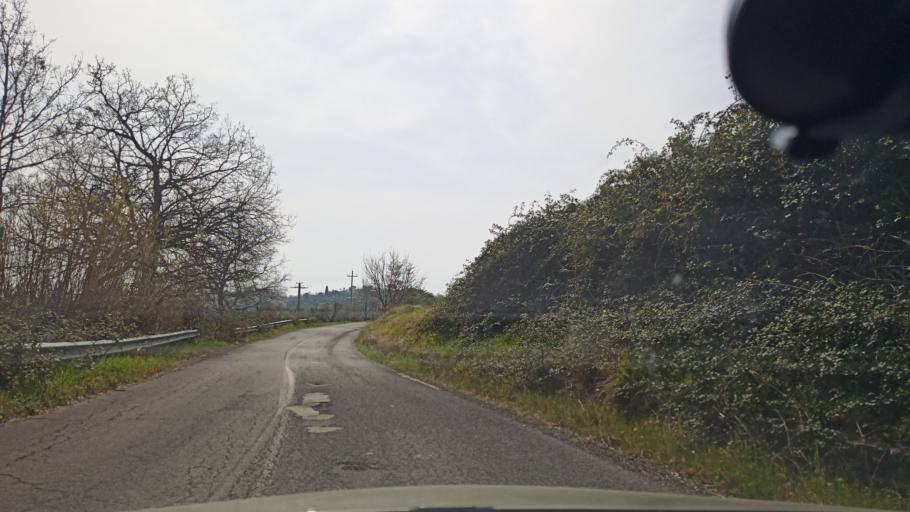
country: IT
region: Latium
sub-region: Provincia di Rieti
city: Torri in Sabina
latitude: 42.3628
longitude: 12.6541
